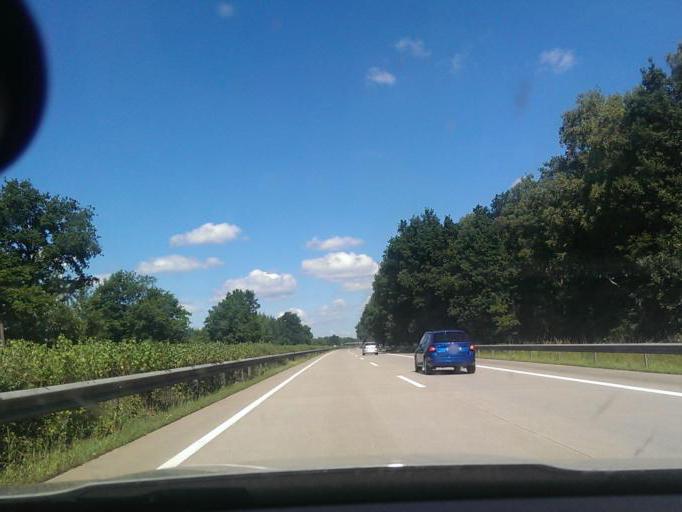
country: DE
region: Lower Saxony
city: Walsrode
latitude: 52.8122
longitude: 9.6238
